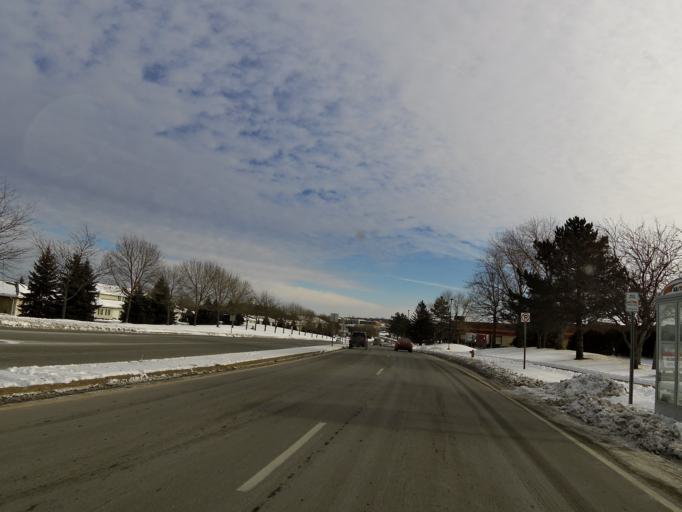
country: US
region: Minnesota
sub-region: Dakota County
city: Burnsville
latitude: 44.7483
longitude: -93.3028
